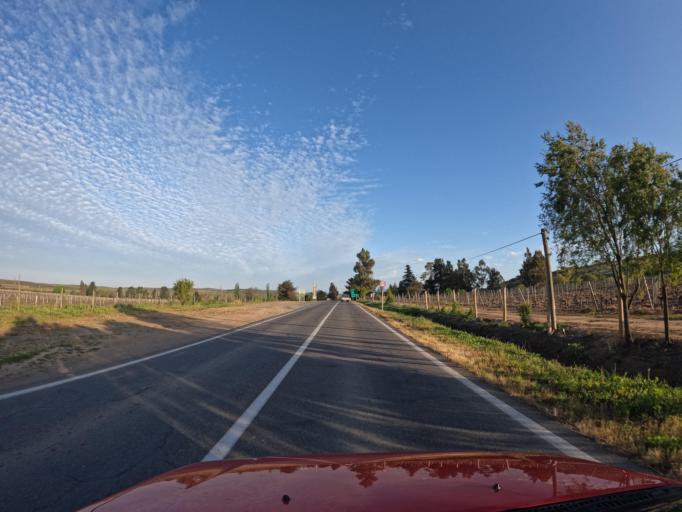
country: CL
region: O'Higgins
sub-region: Provincia de Colchagua
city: Santa Cruz
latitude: -34.2149
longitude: -71.7240
